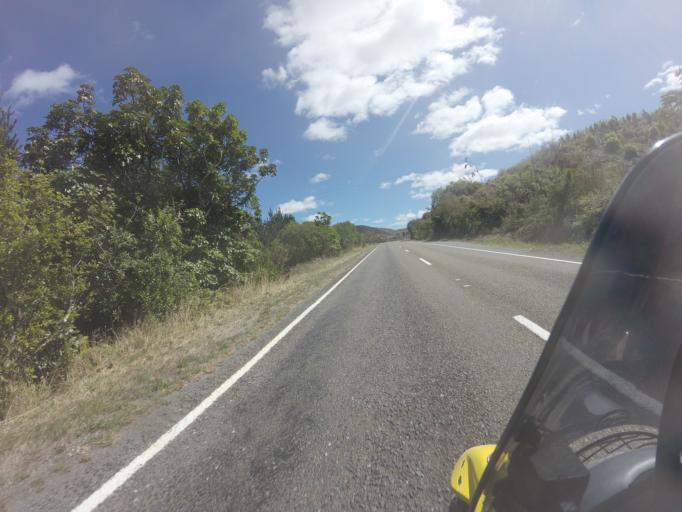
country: NZ
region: Bay of Plenty
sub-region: Kawerau District
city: Kawerau
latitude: -38.1638
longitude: 176.8063
